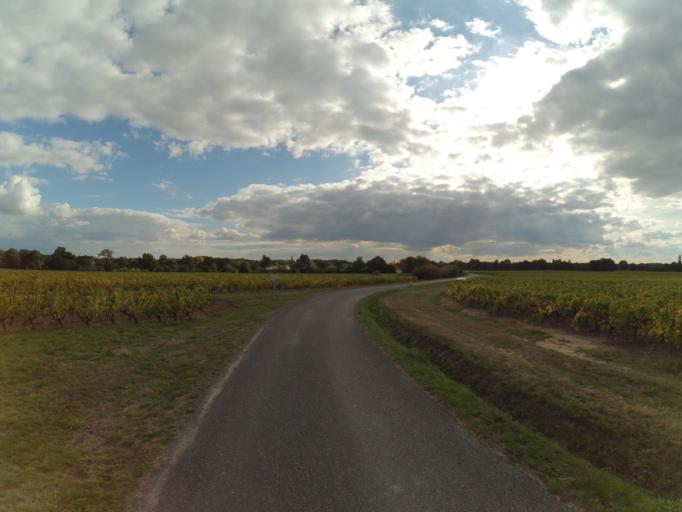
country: FR
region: Pays de la Loire
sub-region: Departement de la Loire-Atlantique
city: Maisdon-sur-Sevre
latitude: 47.0775
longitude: -1.3753
